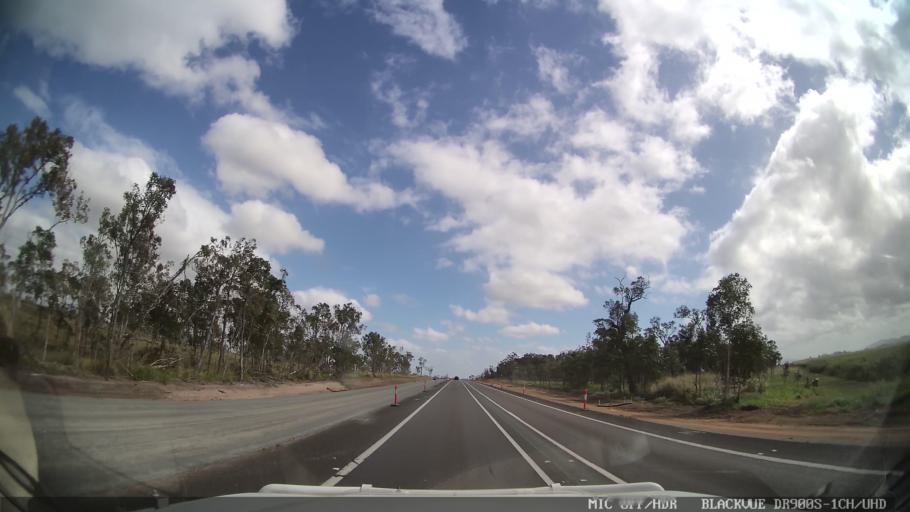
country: AU
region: Queensland
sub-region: Whitsunday
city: Red Hill
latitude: -20.2960
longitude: 148.5044
